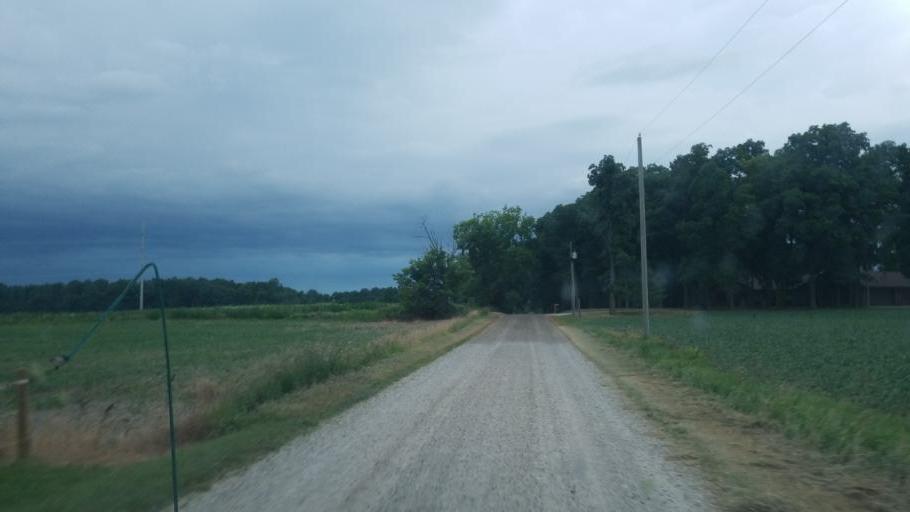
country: US
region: Ohio
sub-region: Defiance County
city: Hicksville
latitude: 41.3289
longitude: -84.8144
